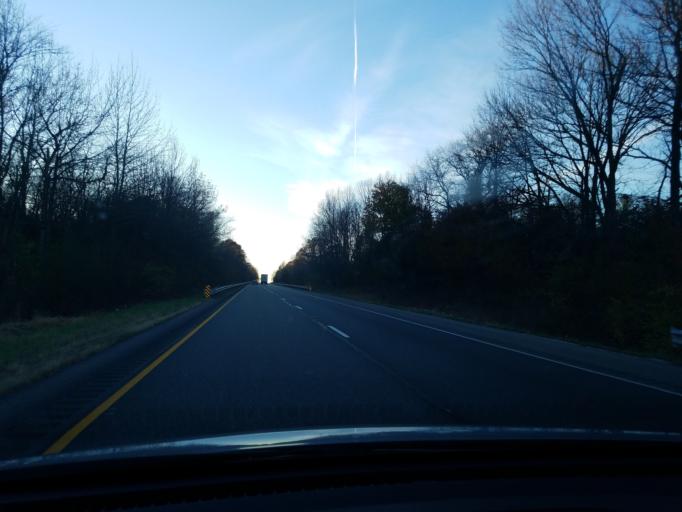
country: US
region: Indiana
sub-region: Gibson County
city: Haubstadt
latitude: 38.1671
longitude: -87.6101
